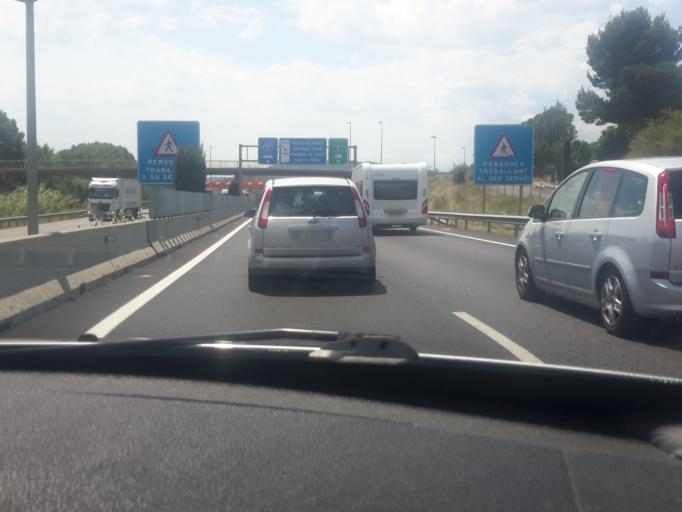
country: ES
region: Catalonia
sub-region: Provincia de Girona
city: la Jonquera
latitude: 42.4146
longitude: 2.8720
